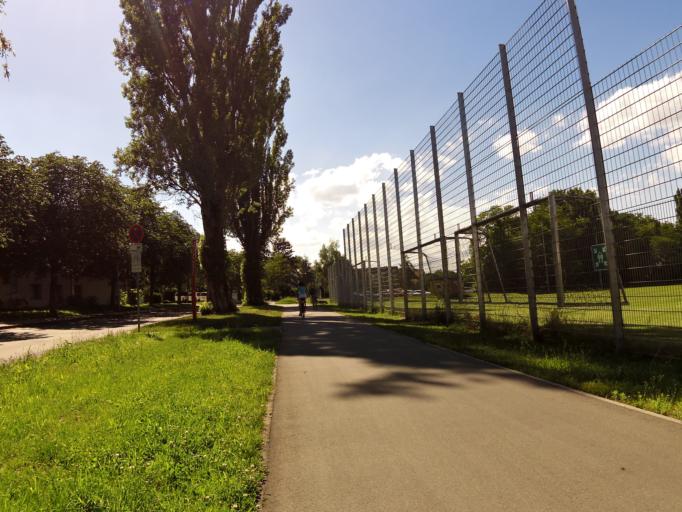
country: DE
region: Baden-Wuerttemberg
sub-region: Freiburg Region
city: Radolfzell am Bodensee
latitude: 47.7366
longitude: 8.9828
